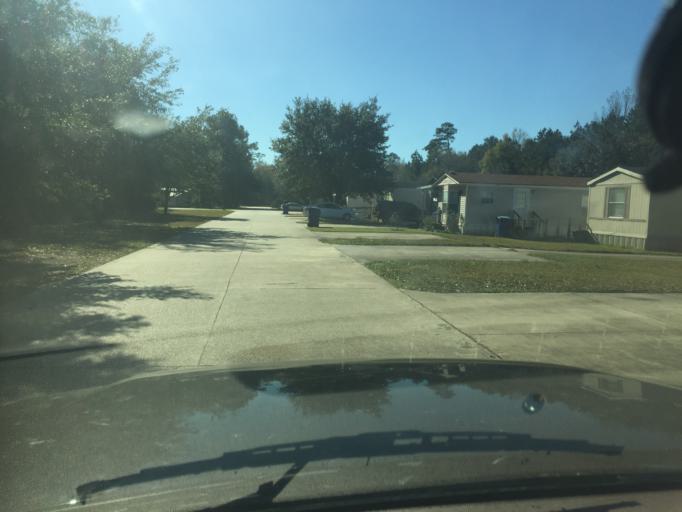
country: US
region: Louisiana
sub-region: Saint Tammany Parish
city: Slidell
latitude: 30.3092
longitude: -89.7336
